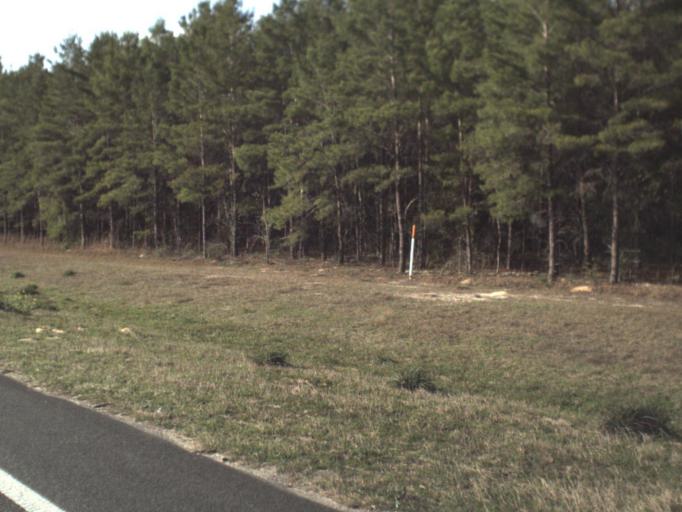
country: US
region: Florida
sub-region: Bay County
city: Lynn Haven
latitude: 30.4356
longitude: -85.6965
